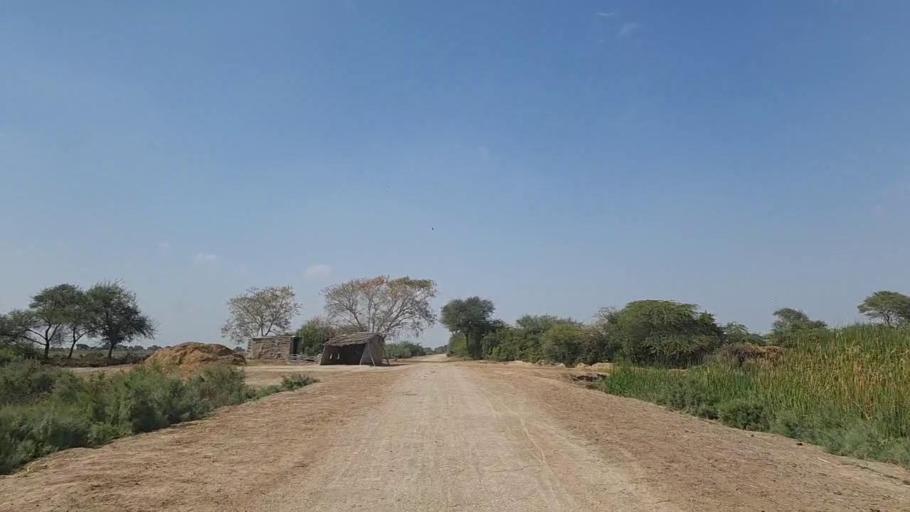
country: PK
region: Sindh
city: Jati
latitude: 24.5122
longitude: 68.2951
